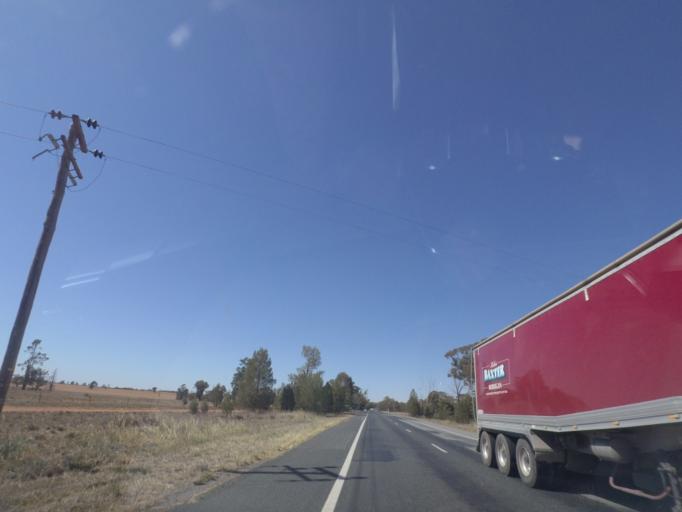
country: AU
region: New South Wales
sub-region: Bland
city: West Wyalong
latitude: -34.1972
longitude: 147.1108
